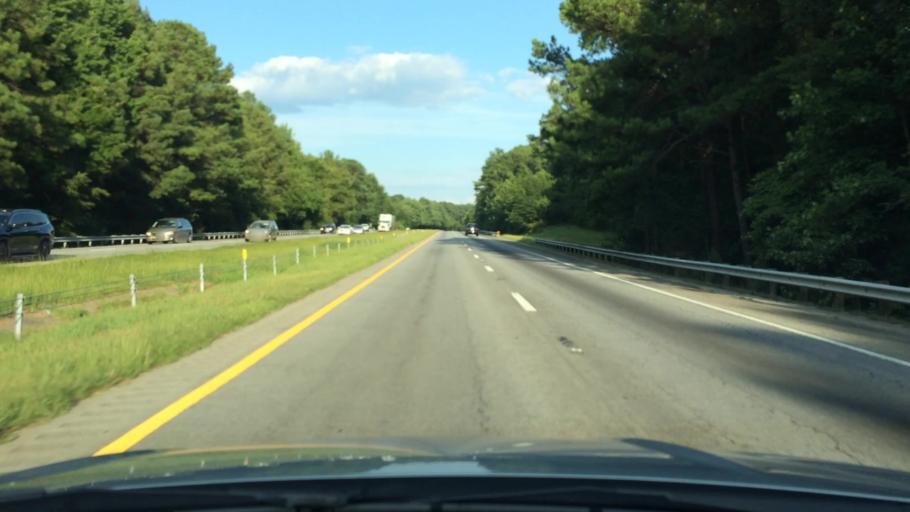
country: US
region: South Carolina
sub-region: Laurens County
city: Joanna
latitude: 34.4279
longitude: -81.7290
